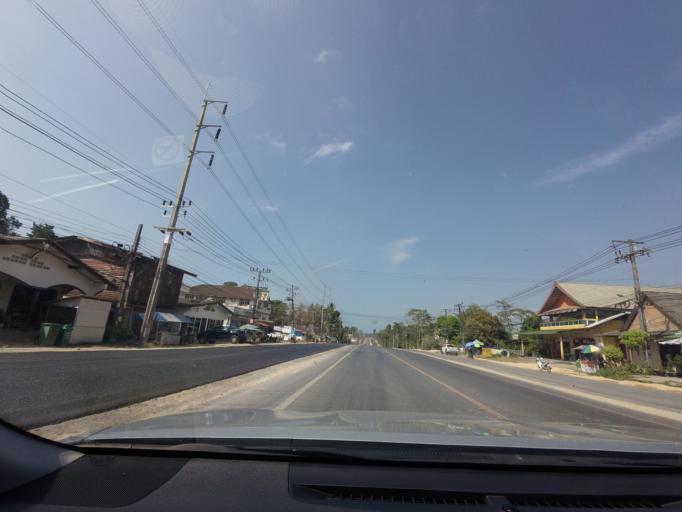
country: TH
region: Phangnga
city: Ban Khao Lak
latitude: 8.7230
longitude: 98.2563
